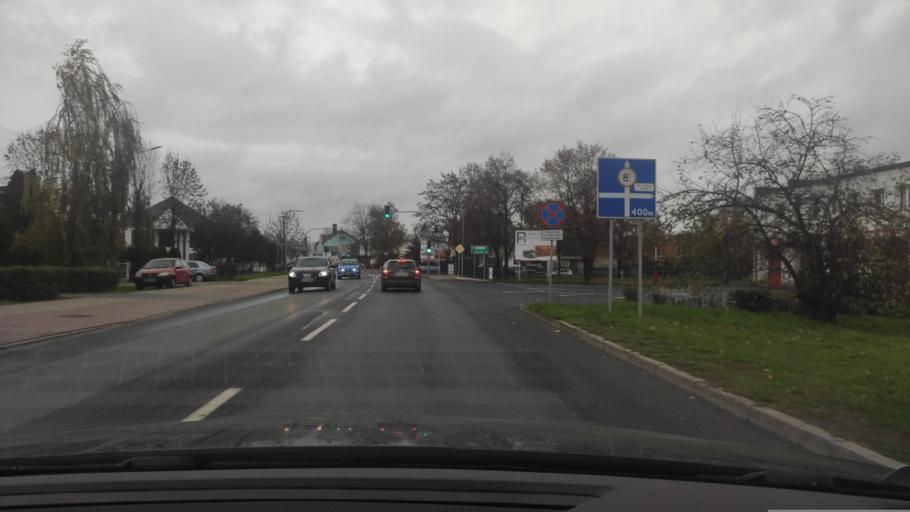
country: PL
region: Greater Poland Voivodeship
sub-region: Powiat poznanski
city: Kostrzyn
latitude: 52.3976
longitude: 17.2172
